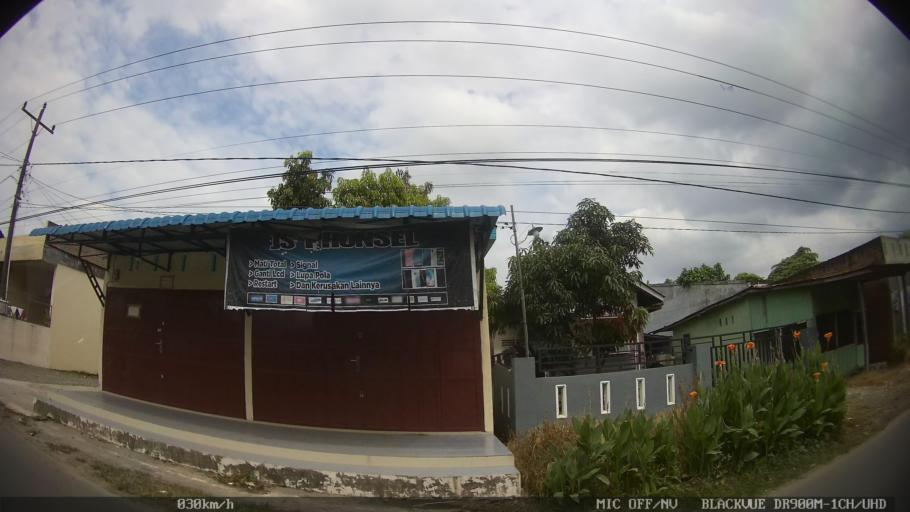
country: ID
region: North Sumatra
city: Sunggal
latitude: 3.6277
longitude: 98.5939
